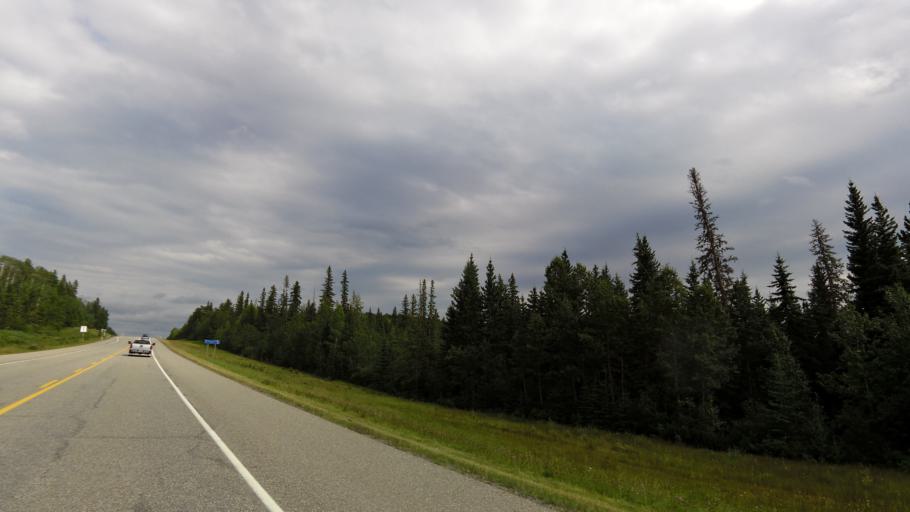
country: CA
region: Alberta
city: Rocky Mountain House
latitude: 52.4698
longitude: -115.7045
